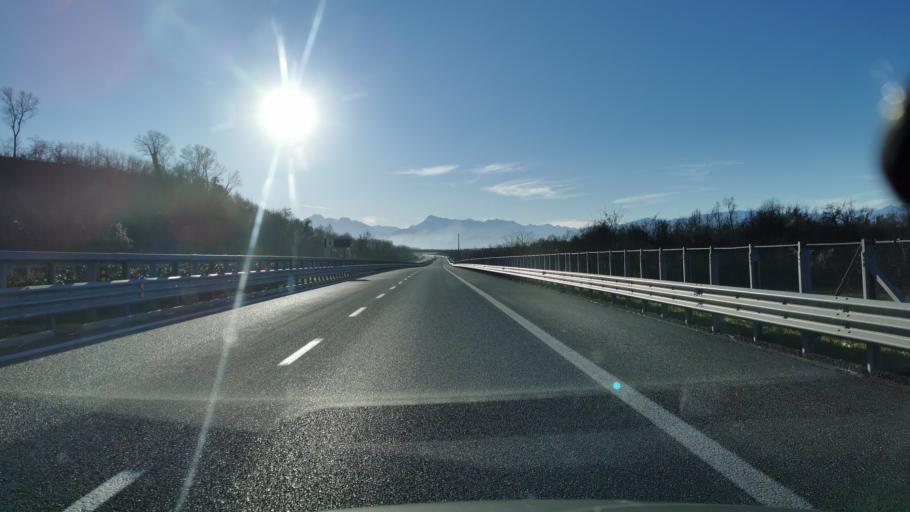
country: IT
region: Piedmont
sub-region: Provincia di Cuneo
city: Castelletto Stura
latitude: 44.4527
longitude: 7.6469
